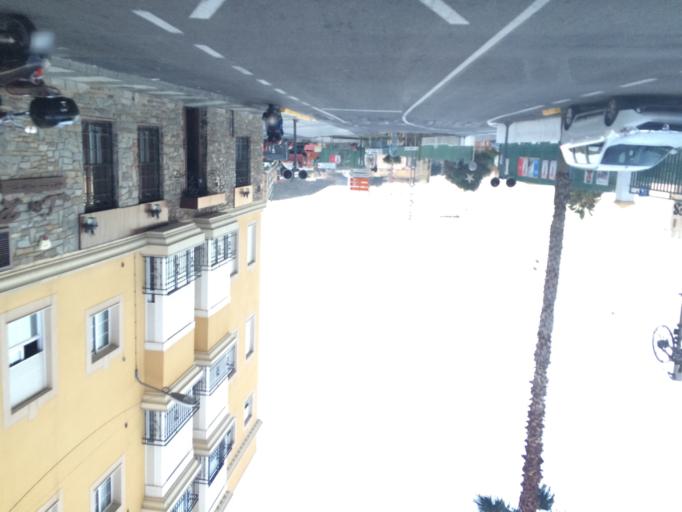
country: ES
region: Andalusia
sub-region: Provincia de Almeria
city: Gador
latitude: 36.9532
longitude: -2.4905
